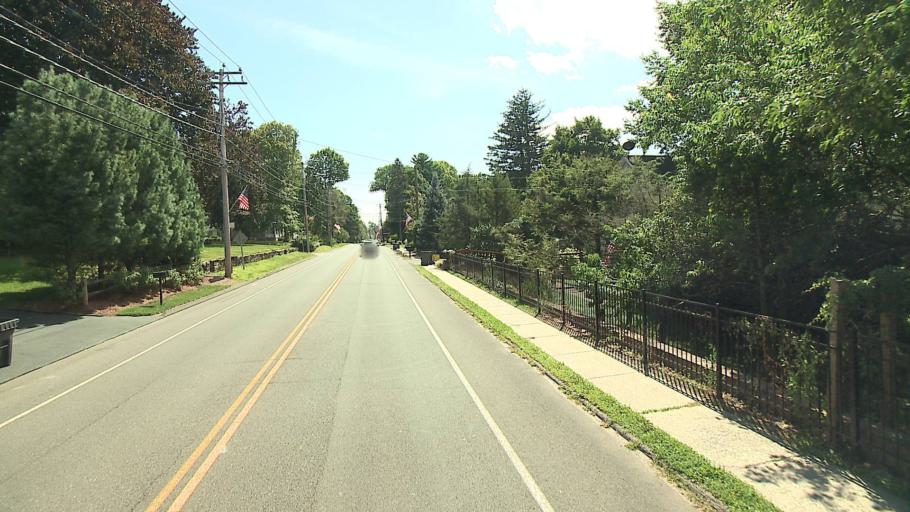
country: US
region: Connecticut
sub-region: Fairfield County
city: Trumbull
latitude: 41.2642
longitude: -73.2232
